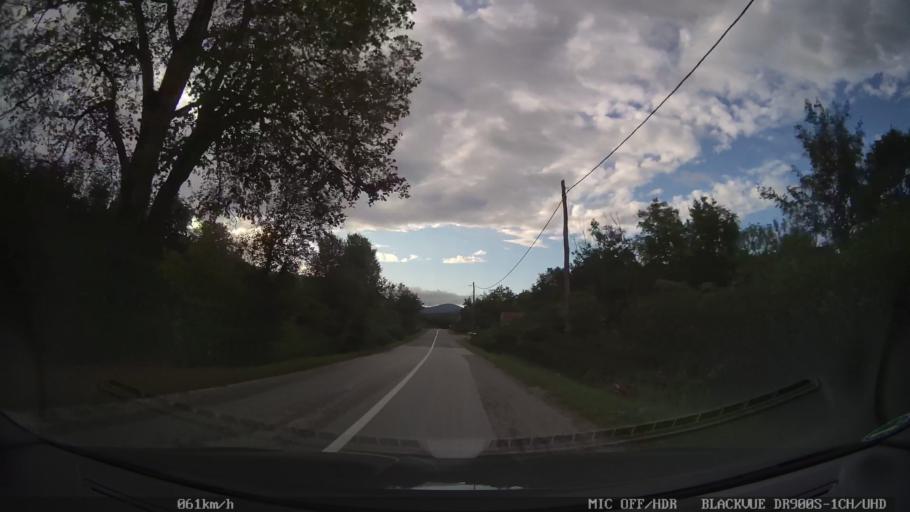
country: HR
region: Karlovacka
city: Plaski
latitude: 44.9937
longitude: 15.4470
